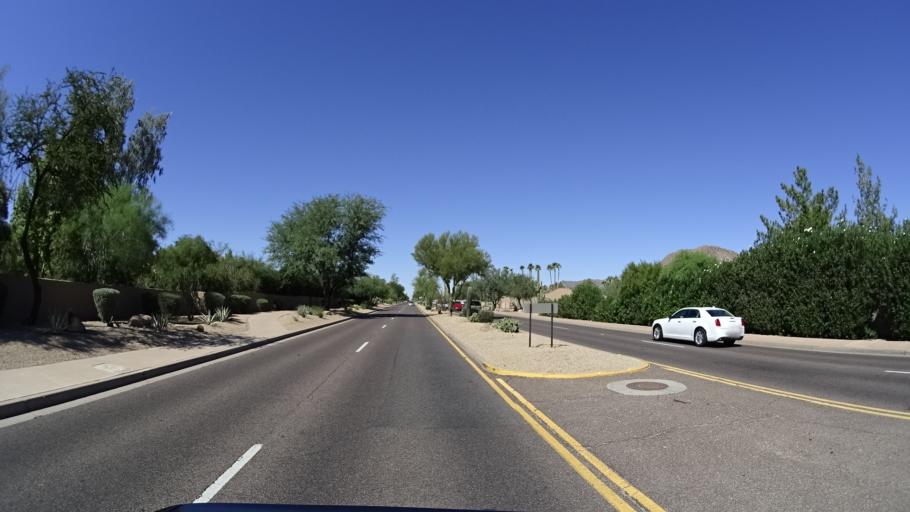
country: US
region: Arizona
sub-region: Maricopa County
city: Paradise Valley
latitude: 33.5313
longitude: -111.9445
